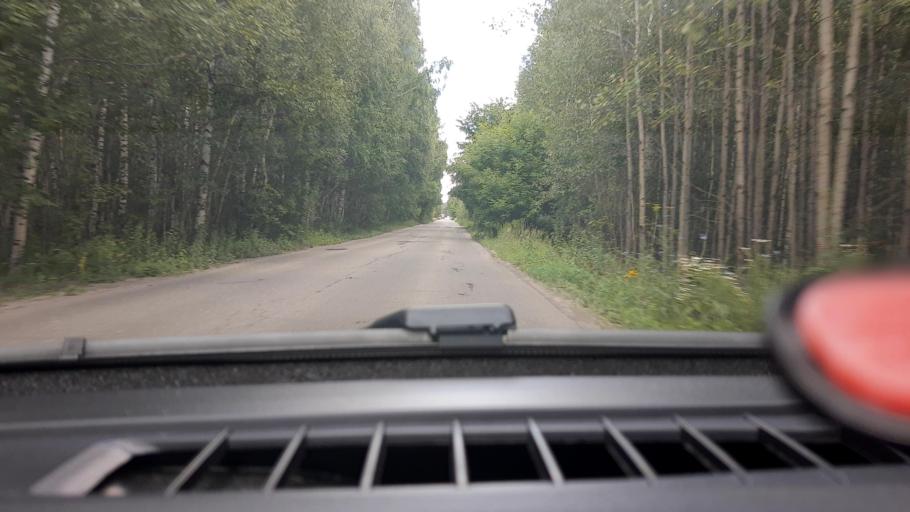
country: RU
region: Nizjnij Novgorod
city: Babino
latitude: 56.3168
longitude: 43.6238
